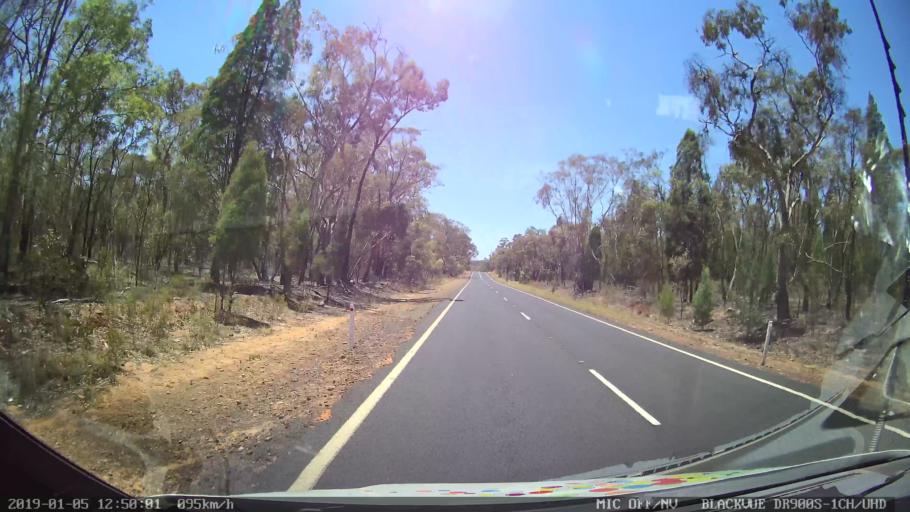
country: AU
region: New South Wales
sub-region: Warrumbungle Shire
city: Coonabarabran
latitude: -31.1183
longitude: 149.6162
